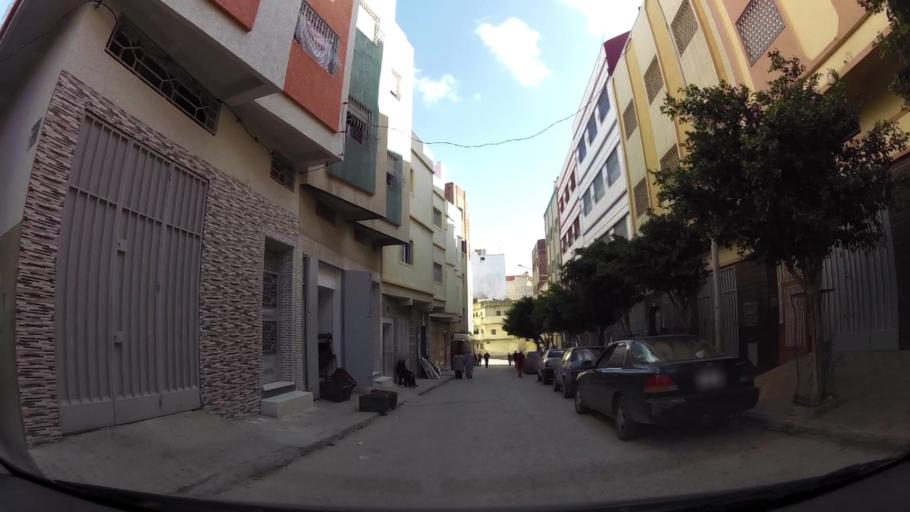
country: MA
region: Tanger-Tetouan
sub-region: Tanger-Assilah
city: Tangier
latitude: 35.7459
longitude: -5.8049
